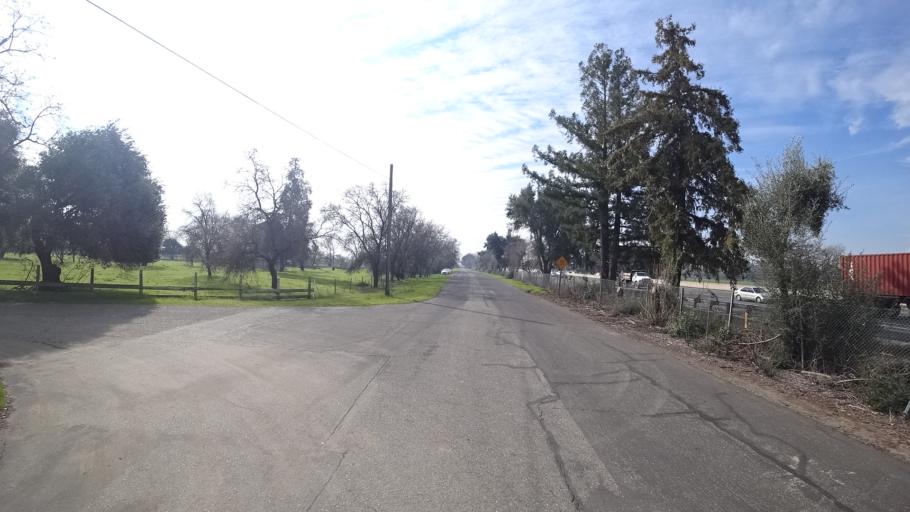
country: US
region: California
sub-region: Yolo County
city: Davis
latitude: 38.5373
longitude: -121.7383
